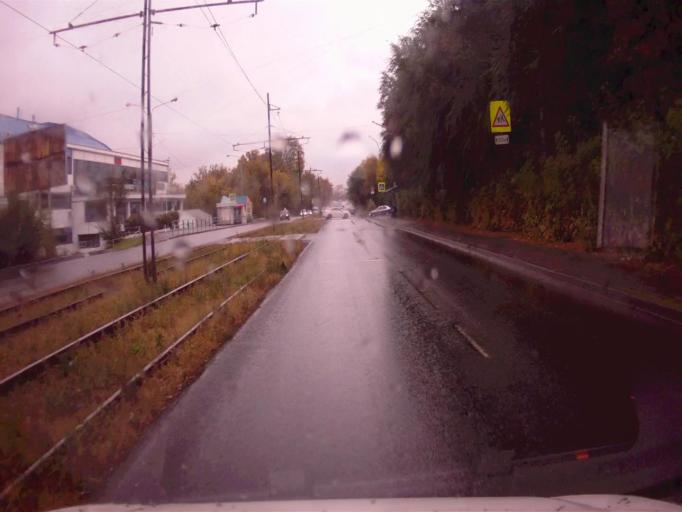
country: RU
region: Chelyabinsk
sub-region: Gorod Chelyabinsk
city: Chelyabinsk
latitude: 55.1771
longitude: 61.4149
